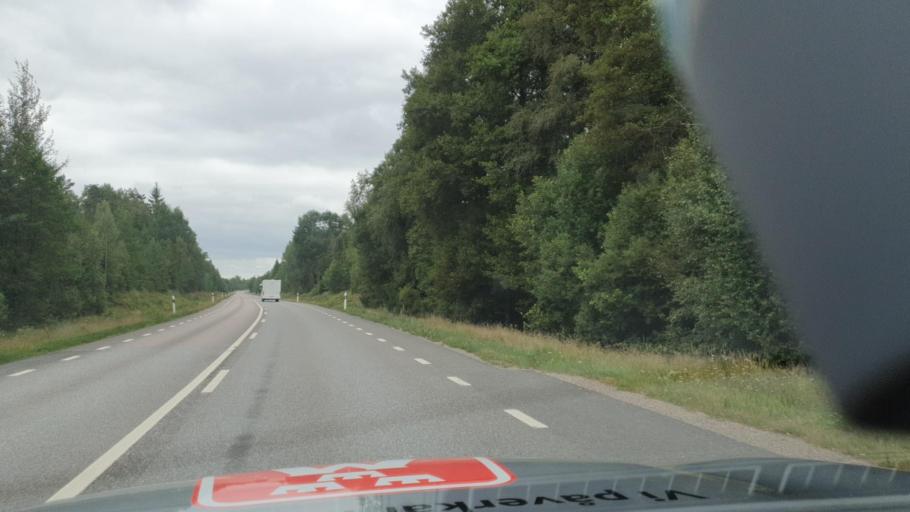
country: SE
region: Kalmar
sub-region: Emmaboda Kommun
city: Emmaboda
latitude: 56.4506
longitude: 15.5661
